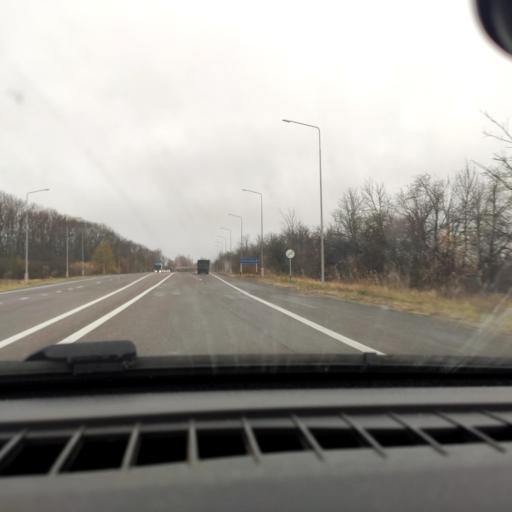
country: RU
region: Voronezj
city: Kolodeznyy
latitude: 51.3349
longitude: 39.0249
